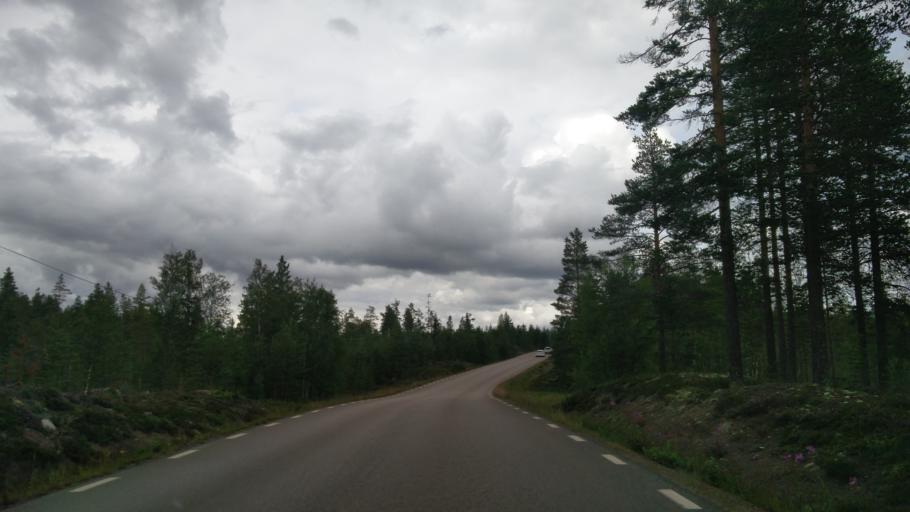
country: NO
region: Hedmark
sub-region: Trysil
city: Innbygda
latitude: 61.1565
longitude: 12.8148
